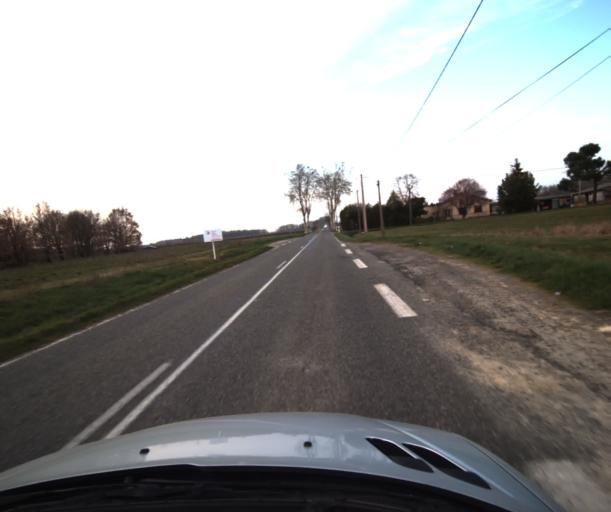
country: FR
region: Midi-Pyrenees
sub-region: Departement de la Haute-Garonne
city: Fronton
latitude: 43.8728
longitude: 1.3795
